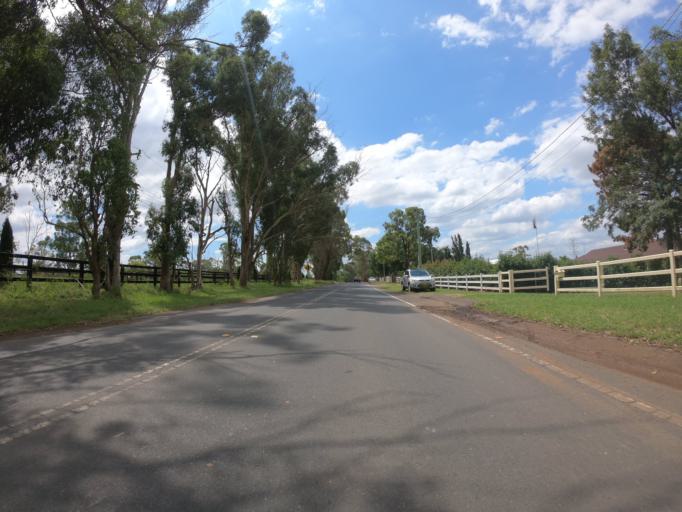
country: AU
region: New South Wales
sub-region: Penrith Municipality
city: Kingswood Park
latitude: -33.8195
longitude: 150.7605
